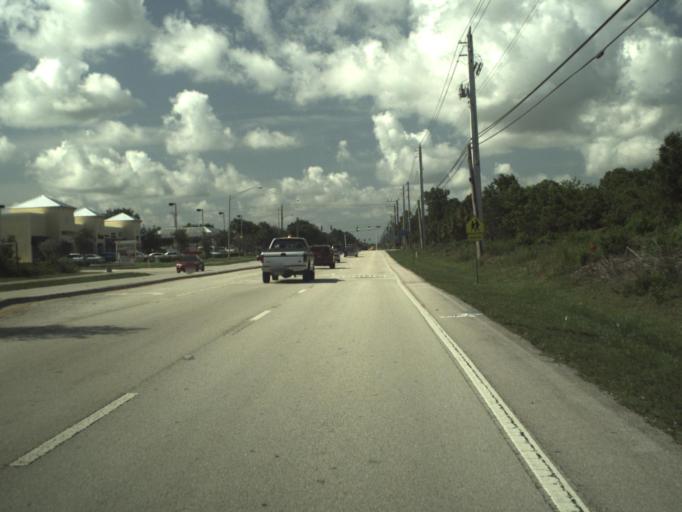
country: US
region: Florida
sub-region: Saint Lucie County
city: Port Saint Lucie
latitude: 27.2529
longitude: -80.3769
